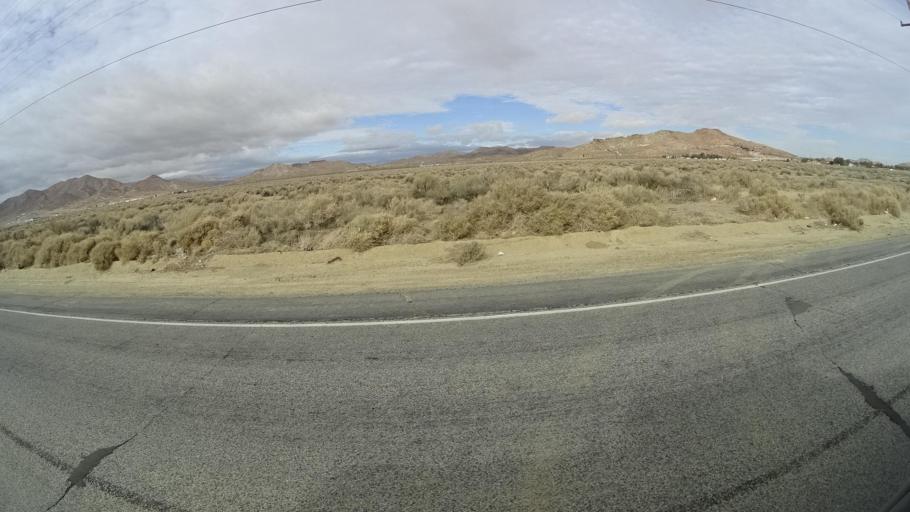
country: US
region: California
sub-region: Kern County
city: Rosamond
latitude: 34.8633
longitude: -118.2452
